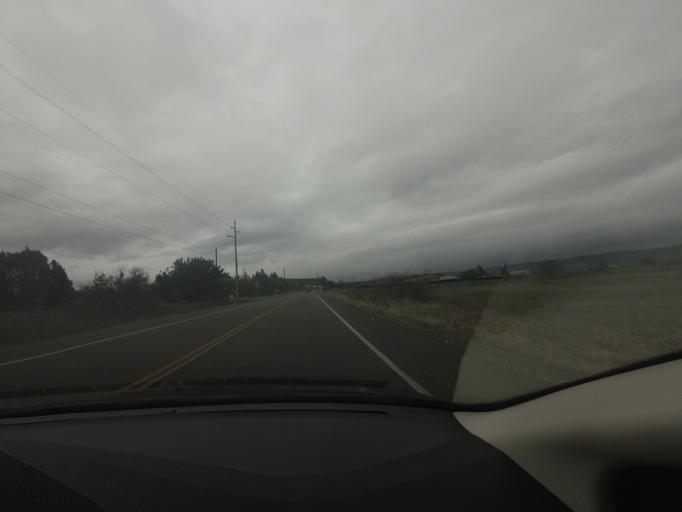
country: US
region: Arizona
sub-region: Yavapai County
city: Lake Montezuma
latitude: 34.6503
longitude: -111.7845
